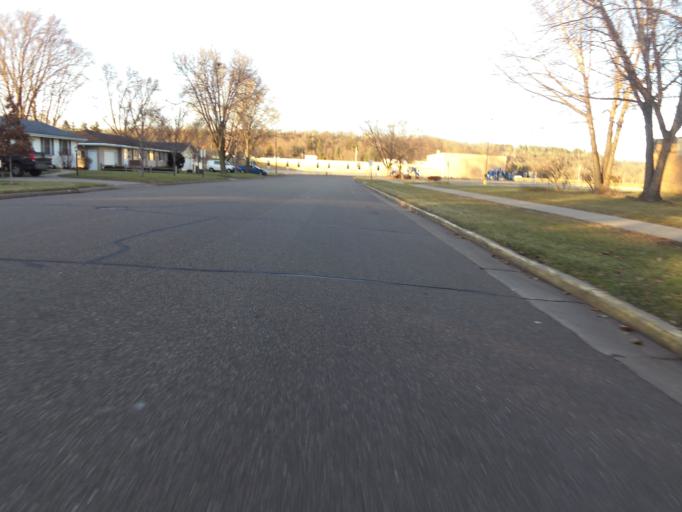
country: US
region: Wisconsin
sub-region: Pierce County
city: River Falls
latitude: 44.8598
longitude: -92.6153
